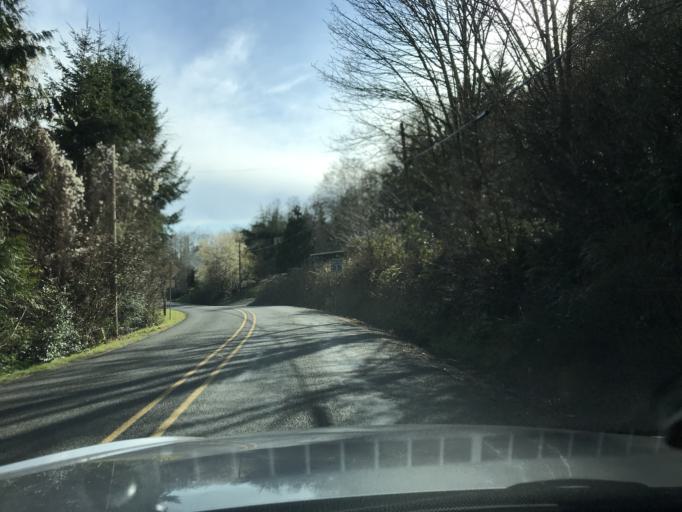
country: US
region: Washington
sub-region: Pierce County
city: Home
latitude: 47.2561
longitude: -122.7588
